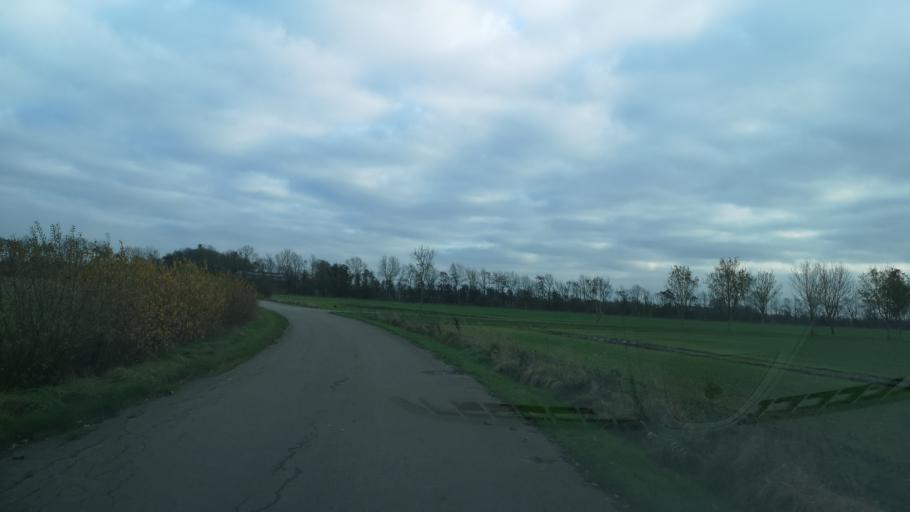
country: DK
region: Central Jutland
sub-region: Ringkobing-Skjern Kommune
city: Videbaek
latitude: 56.0334
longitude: 8.5978
